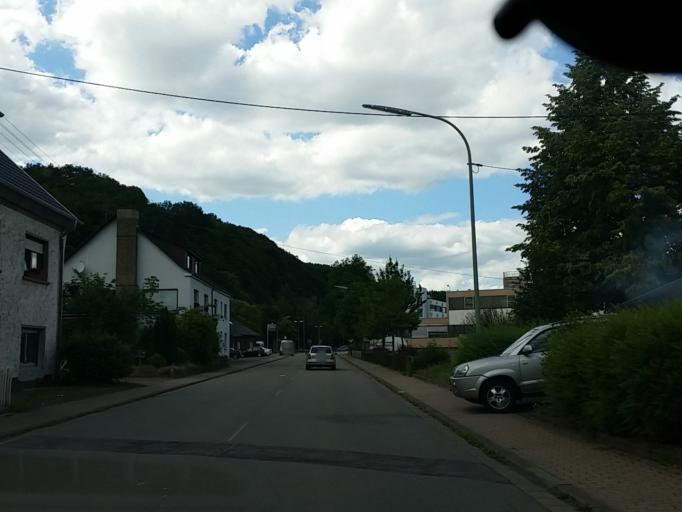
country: DE
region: Saarland
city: Wadern
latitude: 49.4963
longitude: 6.8680
